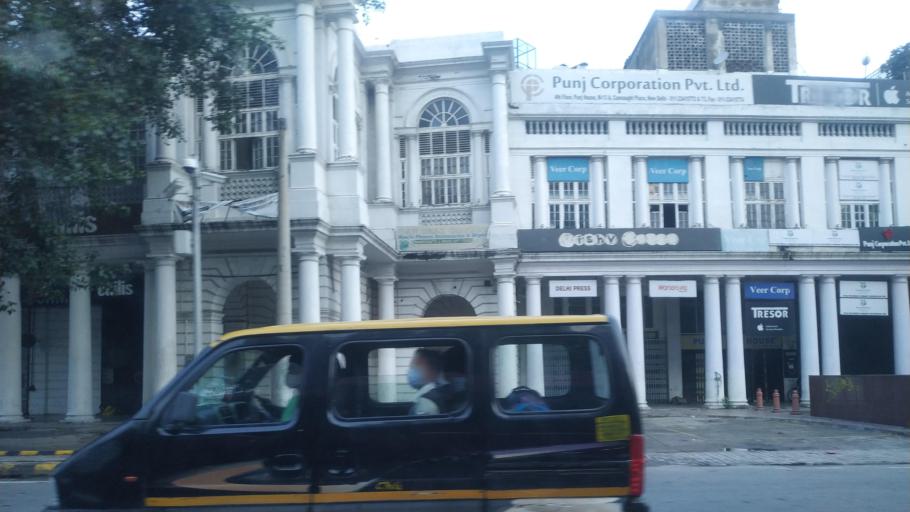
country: IN
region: NCT
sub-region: New Delhi
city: New Delhi
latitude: 28.6316
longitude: 77.2226
